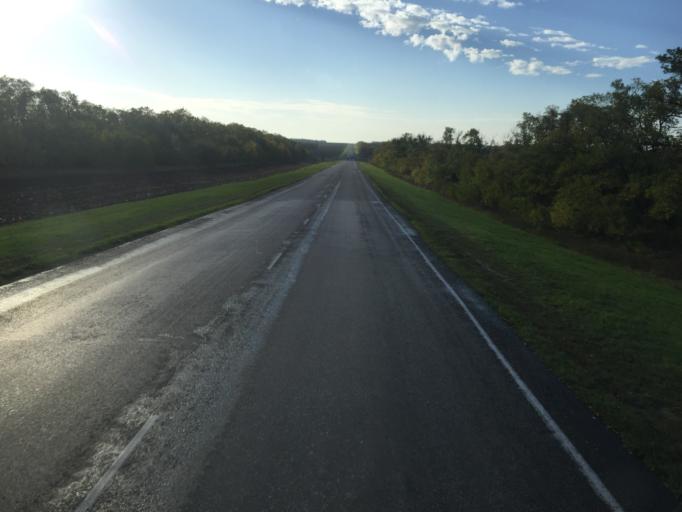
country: RU
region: Rostov
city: Mechetinskaya
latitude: 46.7208
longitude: 40.4873
